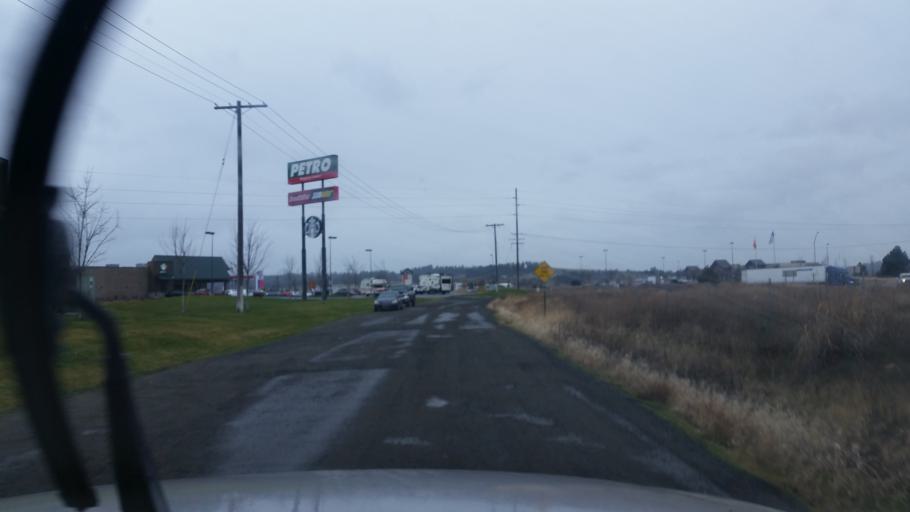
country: US
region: Washington
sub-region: Spokane County
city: Airway Heights
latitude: 47.5920
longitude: -117.5619
